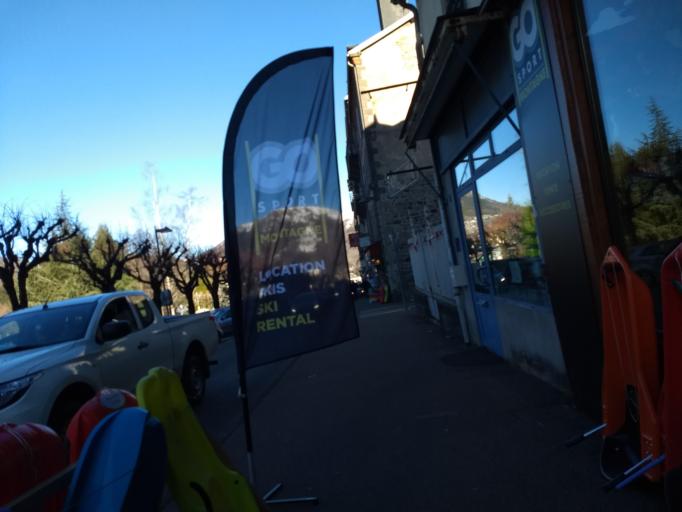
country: FR
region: Auvergne
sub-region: Departement du Puy-de-Dome
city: Mont-Dore
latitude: 45.5723
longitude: 2.8105
